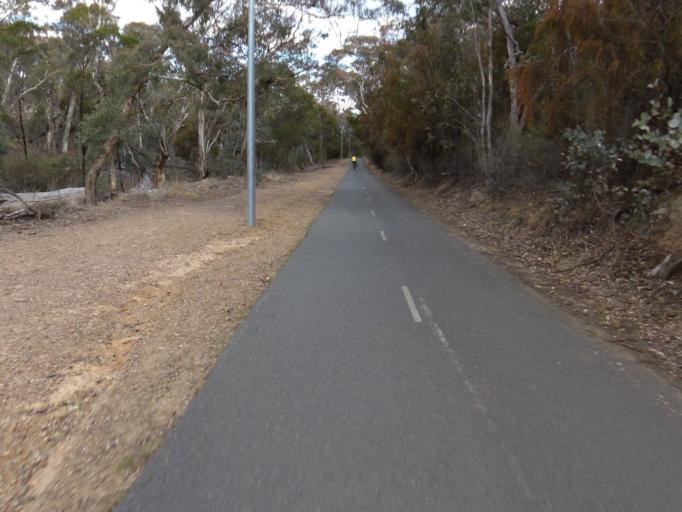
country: AU
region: Australian Capital Territory
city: Acton
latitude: -35.2528
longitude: 149.1082
